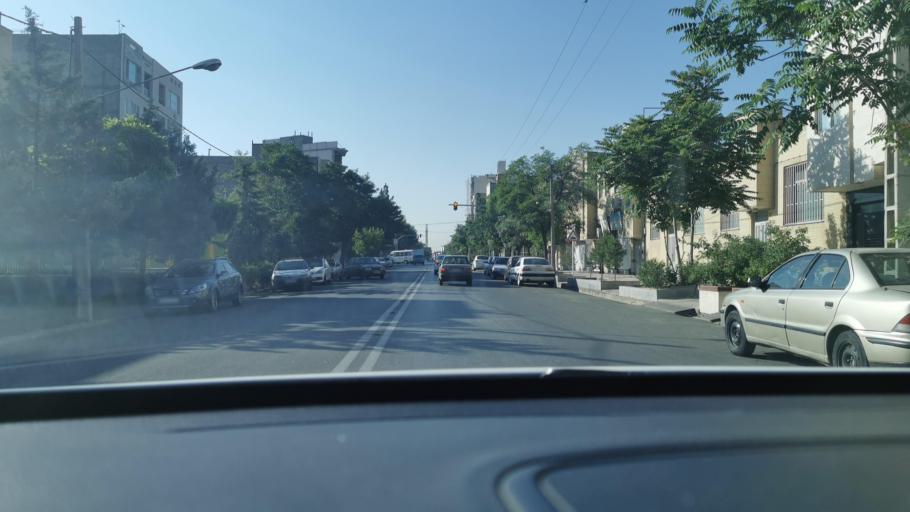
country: IR
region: Razavi Khorasan
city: Mashhad
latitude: 36.3089
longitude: 59.5097
